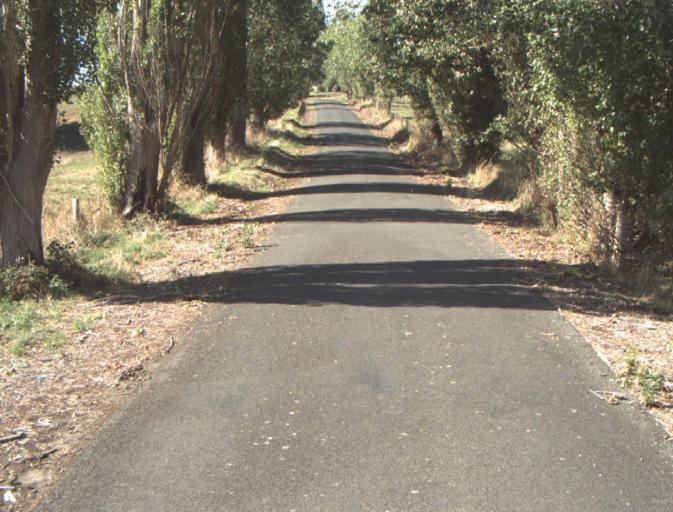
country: AU
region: Tasmania
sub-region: Launceston
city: Mayfield
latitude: -41.2881
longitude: 147.2107
